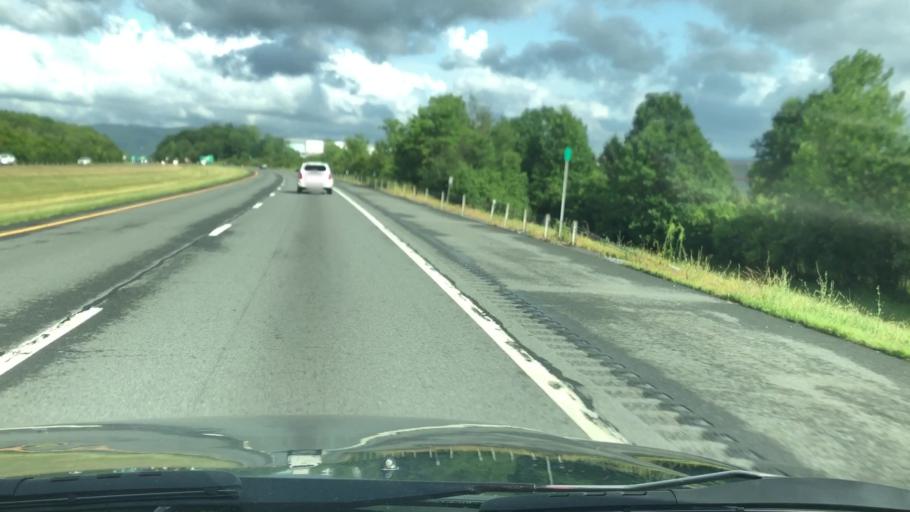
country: US
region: New York
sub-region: Orange County
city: Gardnertown
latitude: 41.5168
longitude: -74.0861
